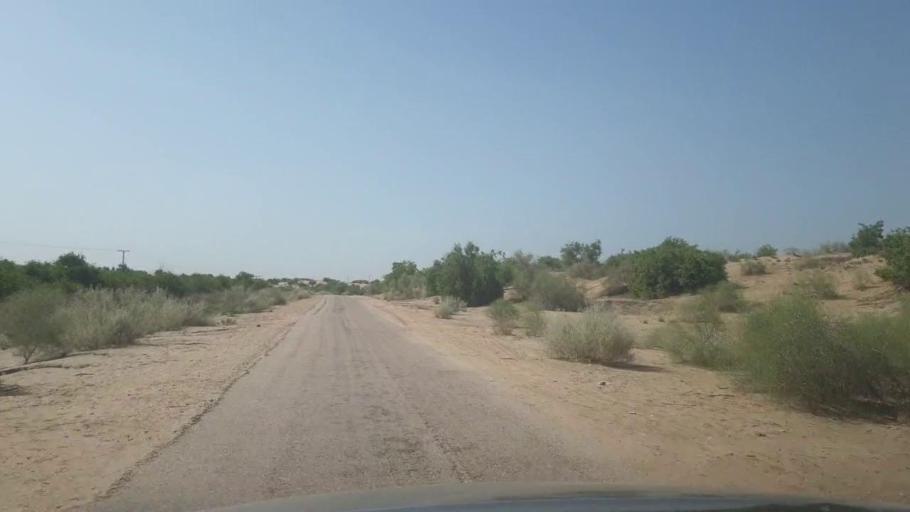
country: PK
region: Sindh
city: Rohri
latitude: 27.4292
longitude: 69.0781
